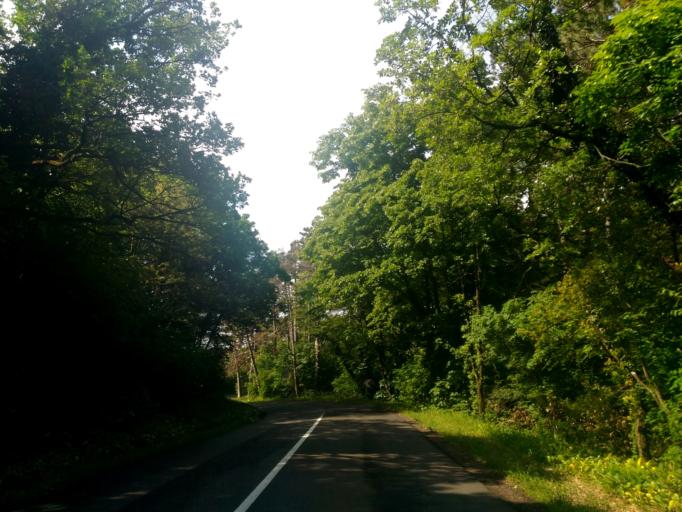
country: HU
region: Baranya
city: Pecs
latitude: 46.1128
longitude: 18.1976
